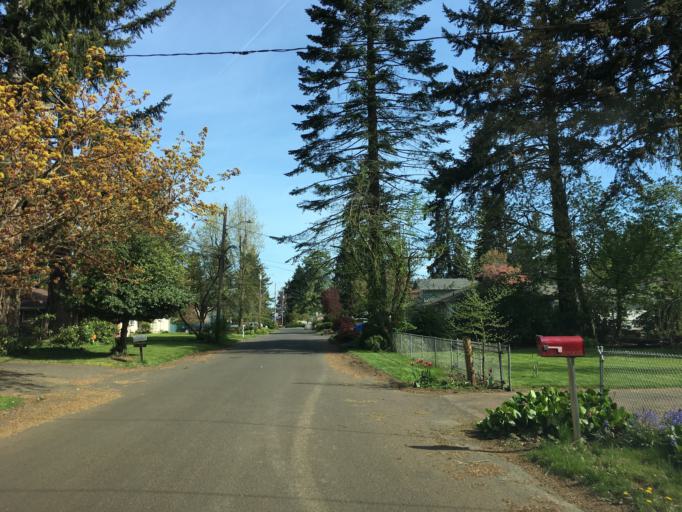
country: US
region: Oregon
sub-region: Multnomah County
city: Lents
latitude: 45.5356
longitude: -122.5192
